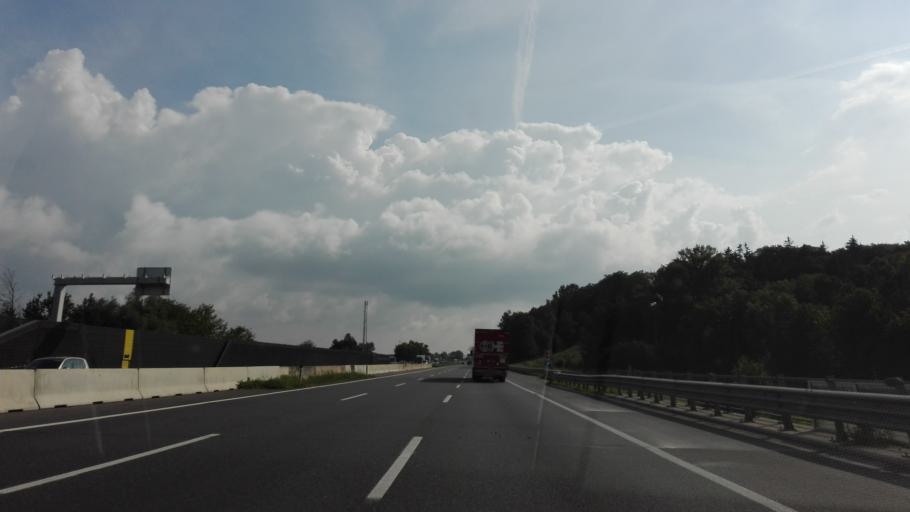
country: AT
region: Lower Austria
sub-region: Politischer Bezirk Melk
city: Ybbs an der Donau
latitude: 48.1519
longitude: 15.0946
